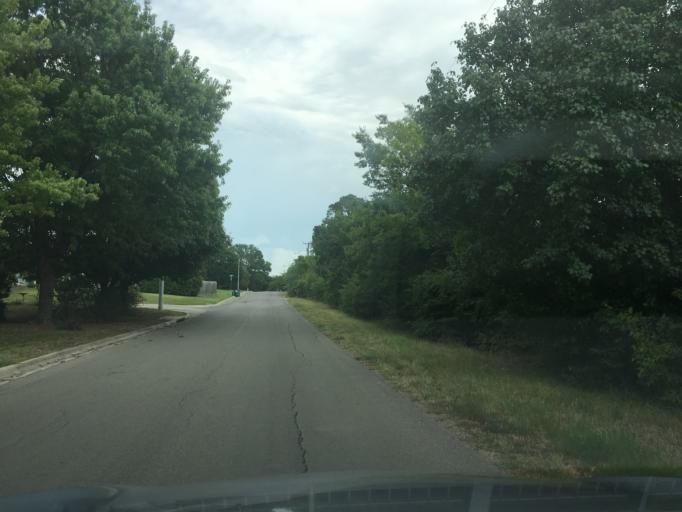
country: US
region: Texas
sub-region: Denton County
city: Denton
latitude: 33.1907
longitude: -97.1587
